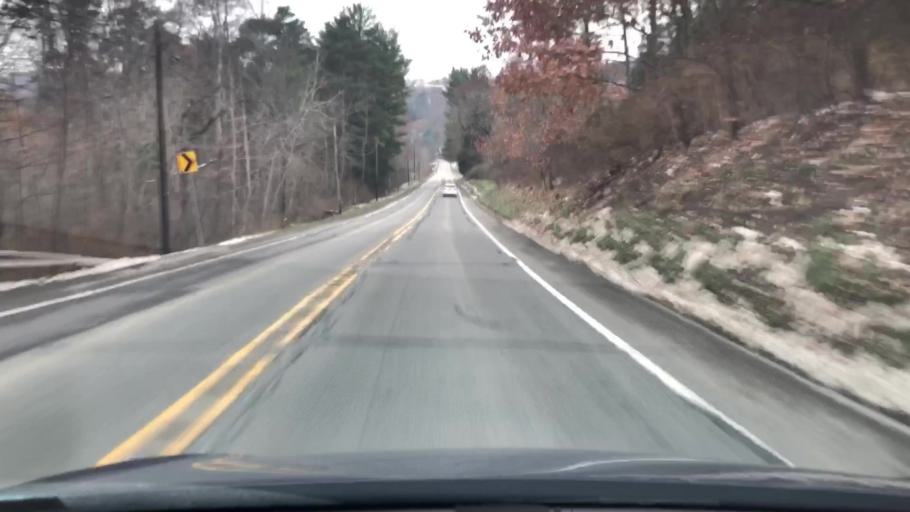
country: US
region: Pennsylvania
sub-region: Jefferson County
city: Brookville
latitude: 41.1271
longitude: -79.1666
